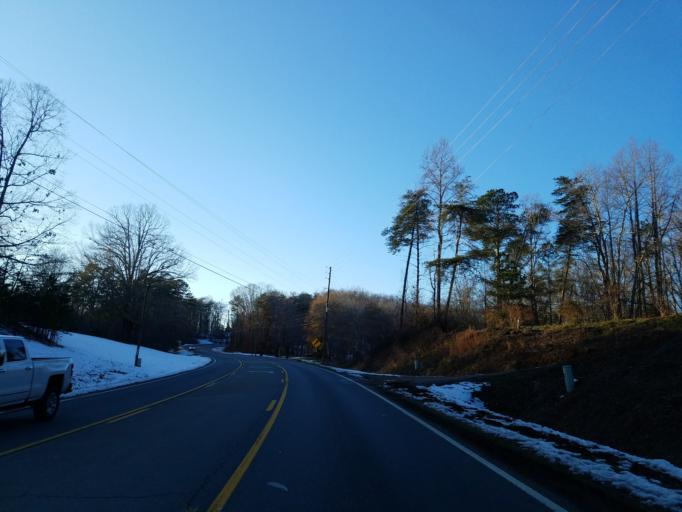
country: US
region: Georgia
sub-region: Dawson County
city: Dawsonville
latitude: 34.3917
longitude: -84.0847
